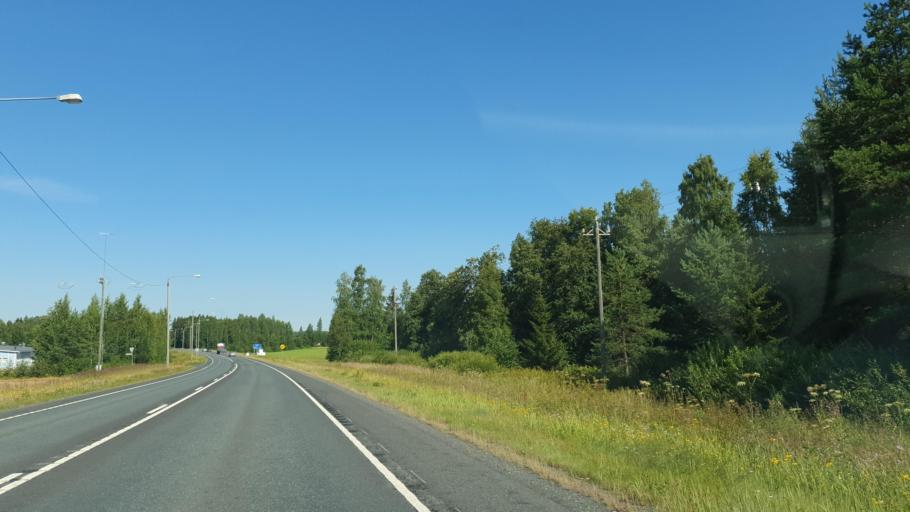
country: FI
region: Northern Savo
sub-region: Kuopio
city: Siilinjaervi
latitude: 63.2045
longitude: 27.5366
